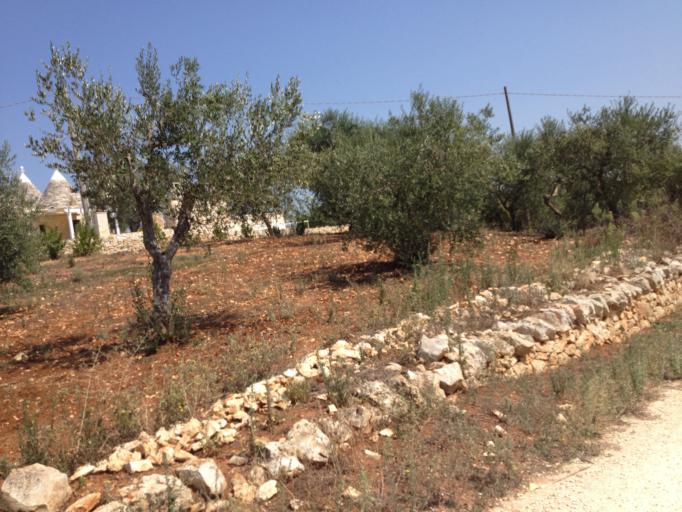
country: IT
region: Apulia
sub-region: Provincia di Brindisi
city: Cisternino
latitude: 40.7190
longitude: 17.4021
